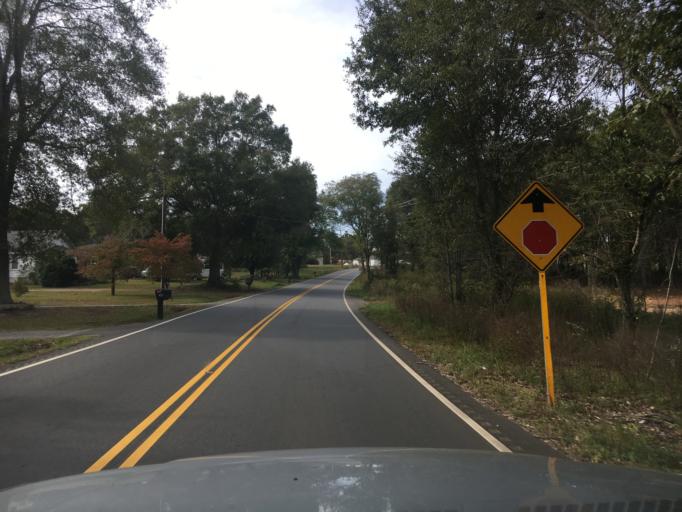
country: US
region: South Carolina
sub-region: Spartanburg County
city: Duncan
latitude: 34.8901
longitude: -82.1386
